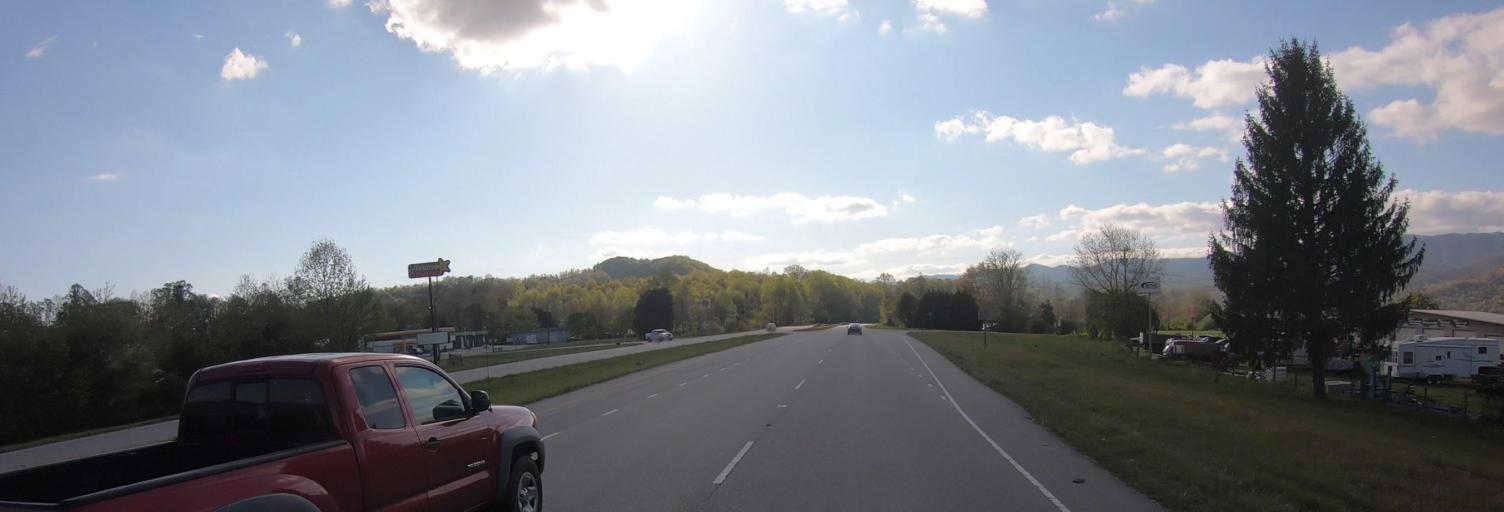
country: US
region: North Carolina
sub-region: Cherokee County
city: Andrews
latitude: 35.1984
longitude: -83.7982
